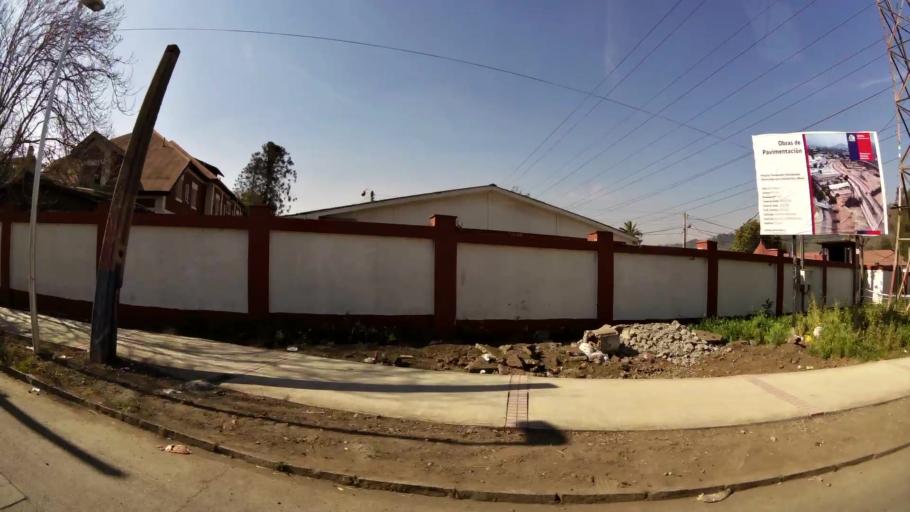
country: CL
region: Santiago Metropolitan
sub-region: Provincia de Santiago
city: Santiago
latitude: -33.4083
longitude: -70.6340
